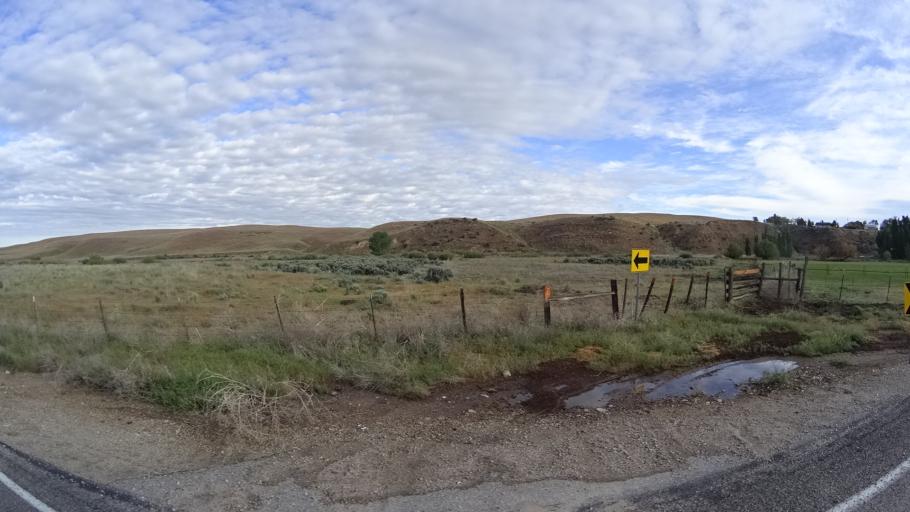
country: US
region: Idaho
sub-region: Ada County
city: Star
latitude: 43.7717
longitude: -116.4932
